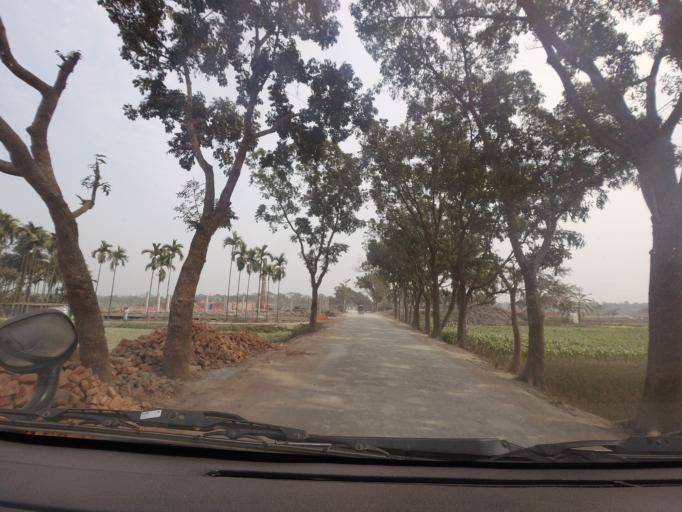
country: BD
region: Dhaka
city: Kishorganj
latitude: 24.3449
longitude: 90.7623
